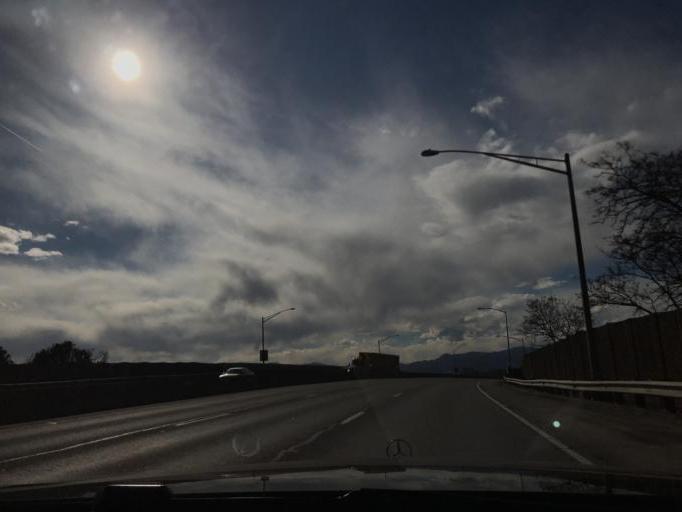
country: US
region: Colorado
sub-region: Adams County
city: Berkley
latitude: 39.7836
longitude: -105.0426
